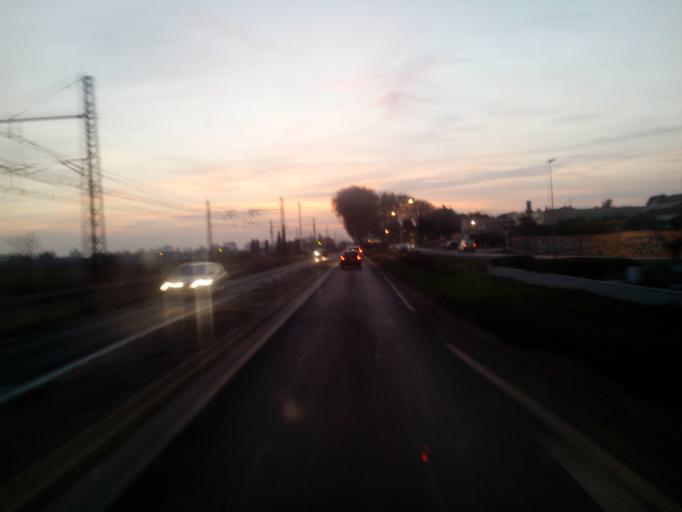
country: FR
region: Languedoc-Roussillon
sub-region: Departement de l'Herault
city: Saint-Bres
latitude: 43.6646
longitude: 4.0377
